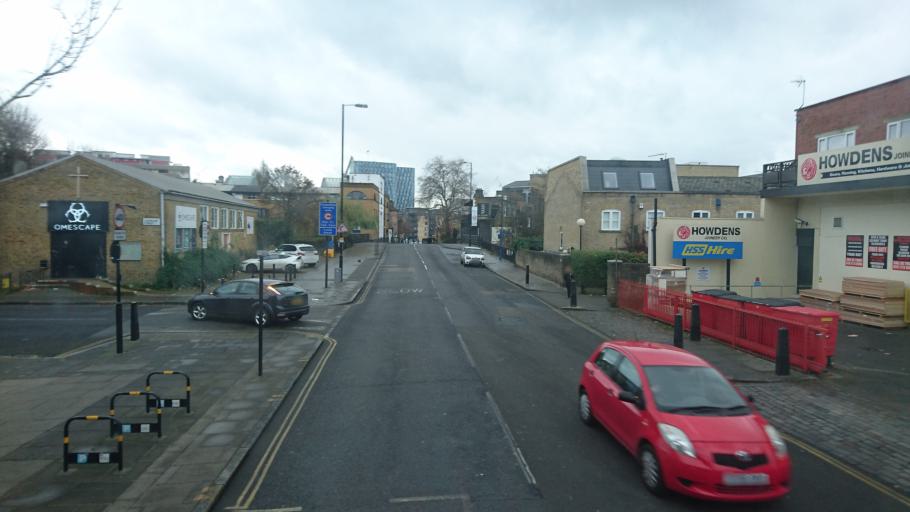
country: GB
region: England
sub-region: Greater London
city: Barnsbury
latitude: 51.5357
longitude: -0.1168
